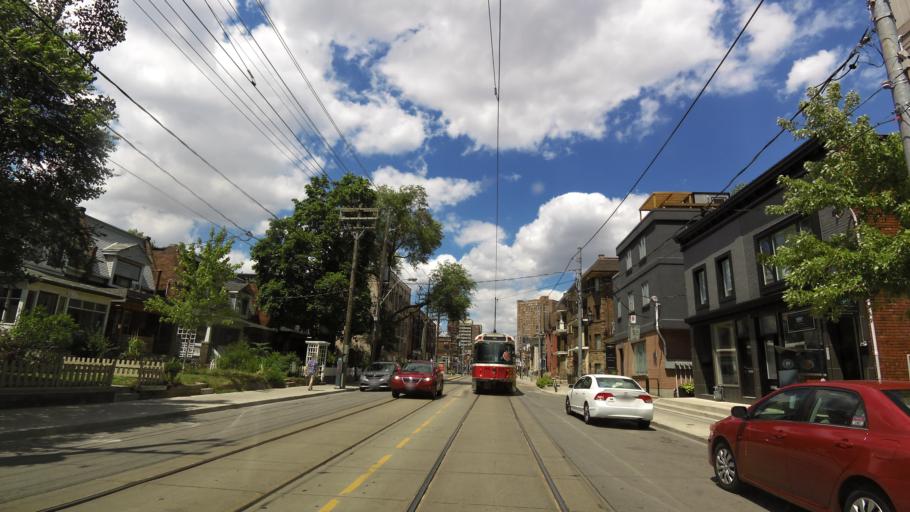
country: CA
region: Ontario
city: Toronto
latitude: 43.6525
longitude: -79.4514
